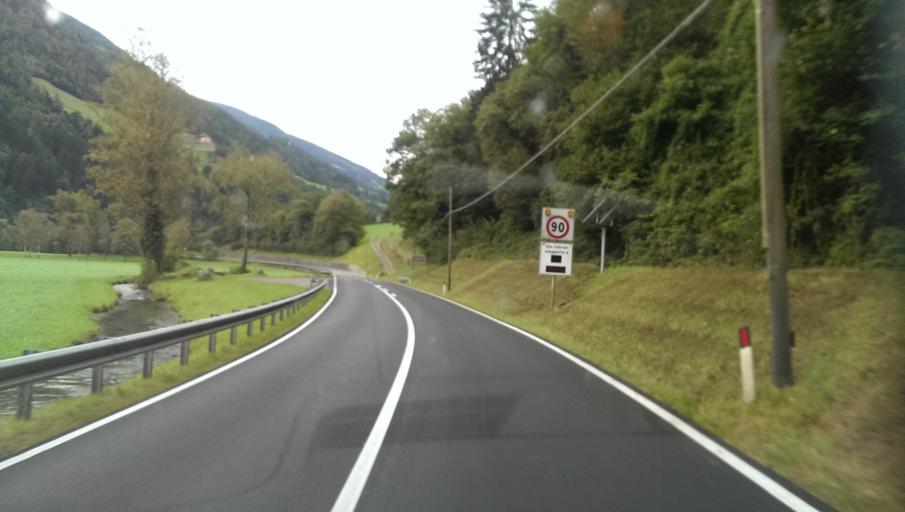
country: IT
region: Trentino-Alto Adige
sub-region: Bolzano
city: San Martino in Passiria
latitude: 46.7516
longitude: 11.2061
